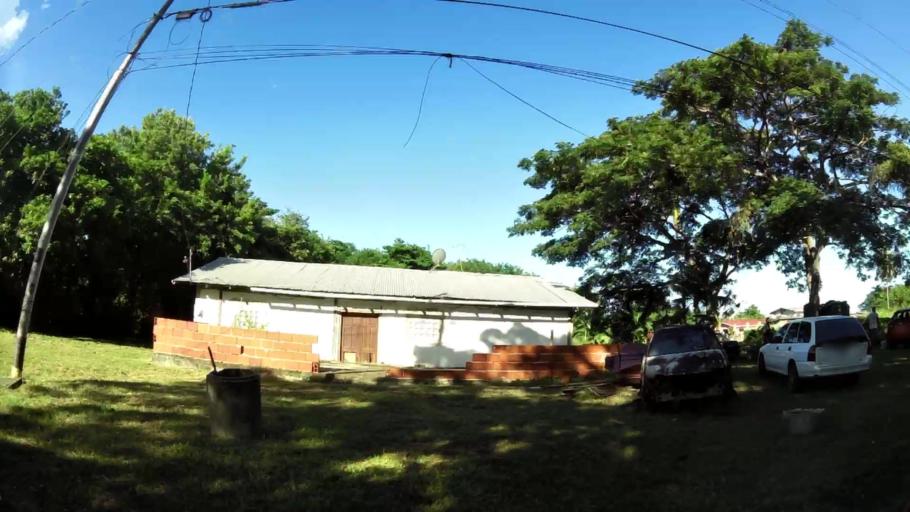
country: TT
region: Tobago
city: Scarborough
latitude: 11.1512
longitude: -60.8237
